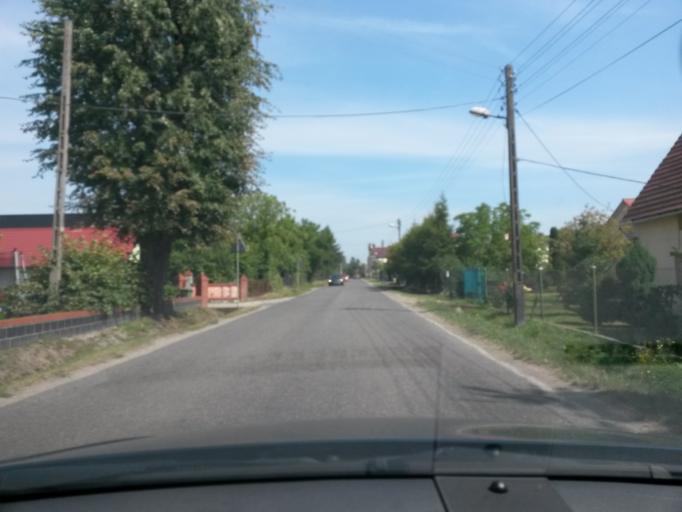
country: PL
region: Lower Silesian Voivodeship
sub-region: Powiat legnicki
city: Prochowice
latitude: 51.2132
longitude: 16.3507
